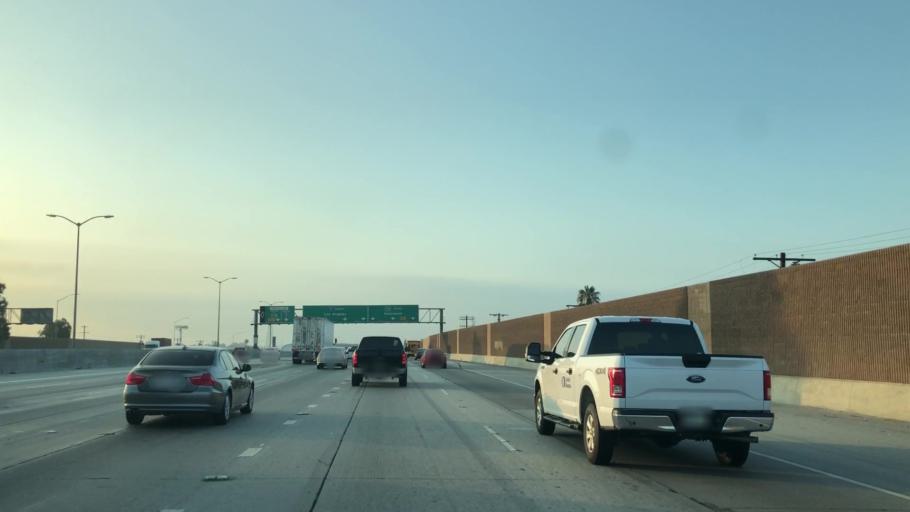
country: US
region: California
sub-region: Los Angeles County
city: San Fernando
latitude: 34.2405
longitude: -118.4171
